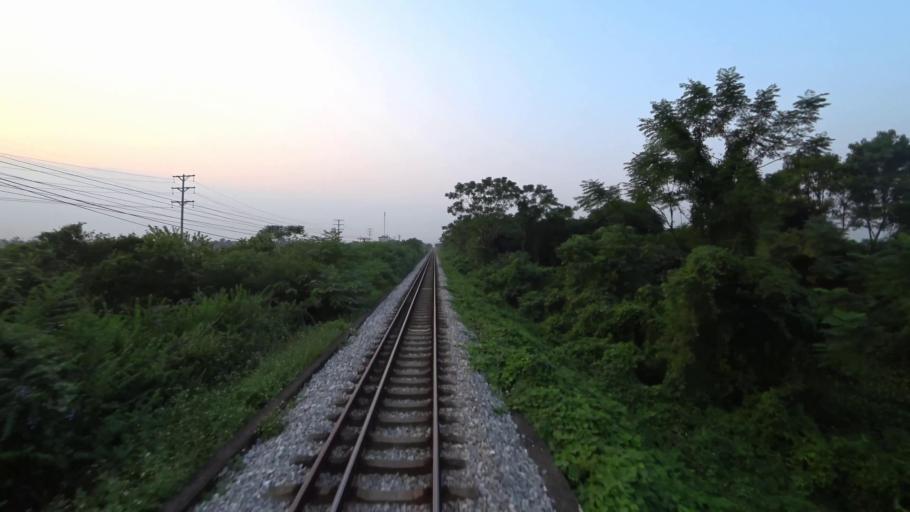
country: VN
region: Ha Noi
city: Dong Anh
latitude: 21.1246
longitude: 105.8819
